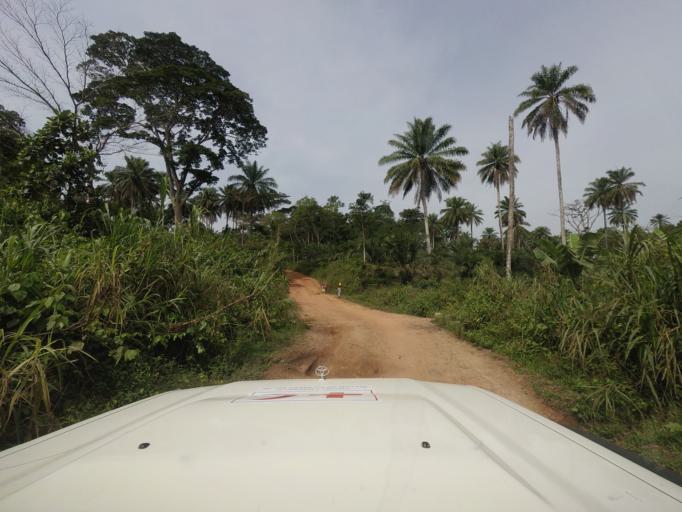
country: GN
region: Nzerekore
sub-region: Macenta
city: Macenta
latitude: 8.4790
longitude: -9.5518
